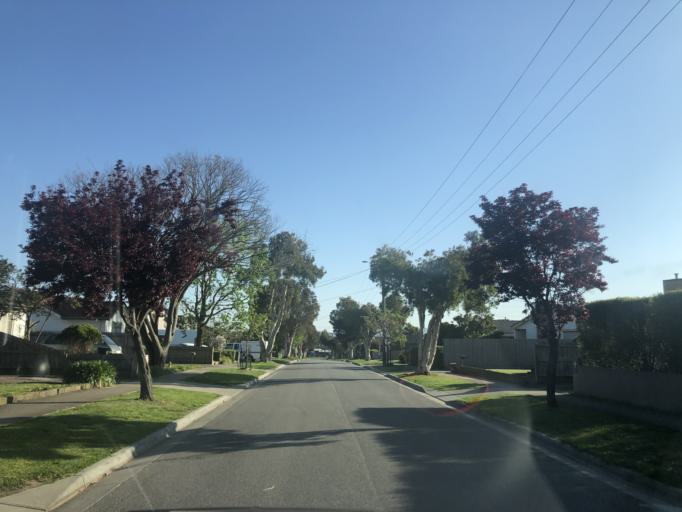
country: AU
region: Victoria
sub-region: Casey
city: Hampton Park
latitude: -38.0335
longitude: 145.2581
